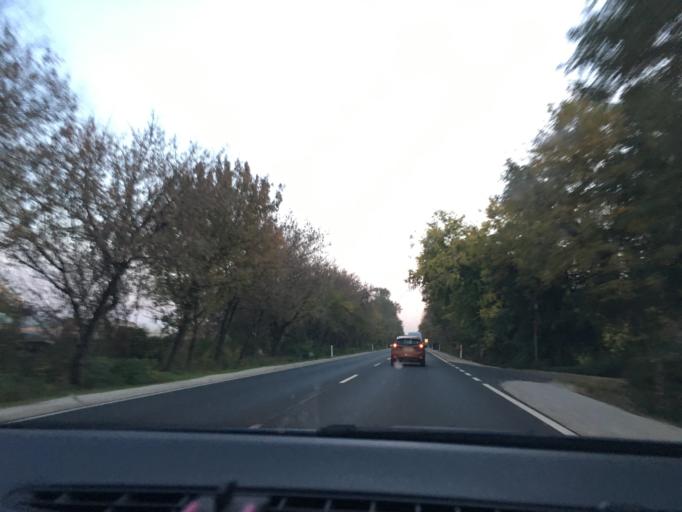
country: HU
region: Hajdu-Bihar
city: Debrecen
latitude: 47.5660
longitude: 21.6521
